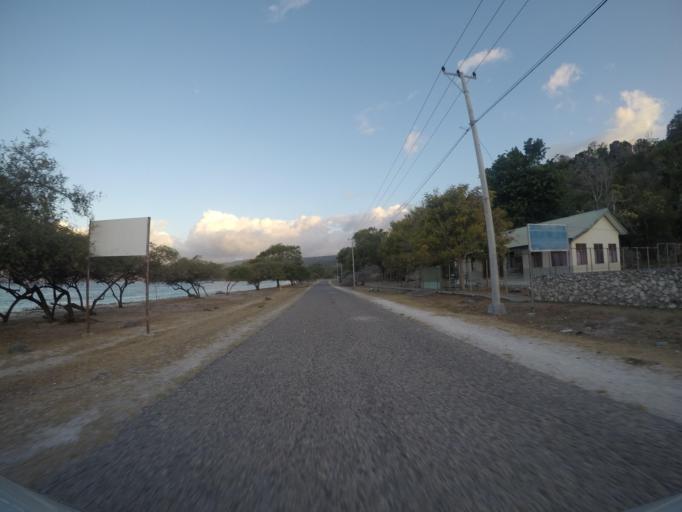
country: TL
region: Lautem
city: Lospalos
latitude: -8.3509
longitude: 127.0524
